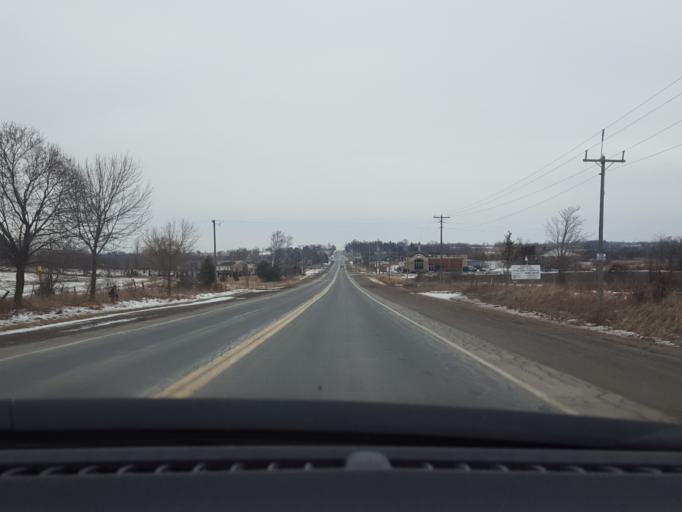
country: CA
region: Ontario
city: Newmarket
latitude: 44.1339
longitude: -79.4234
